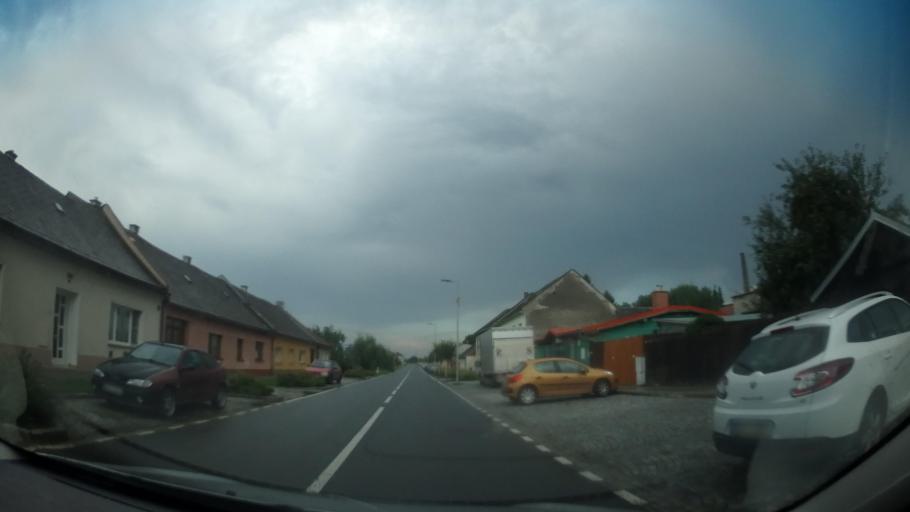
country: CZ
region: Olomoucky
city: Lostice
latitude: 49.7418
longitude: 16.9386
